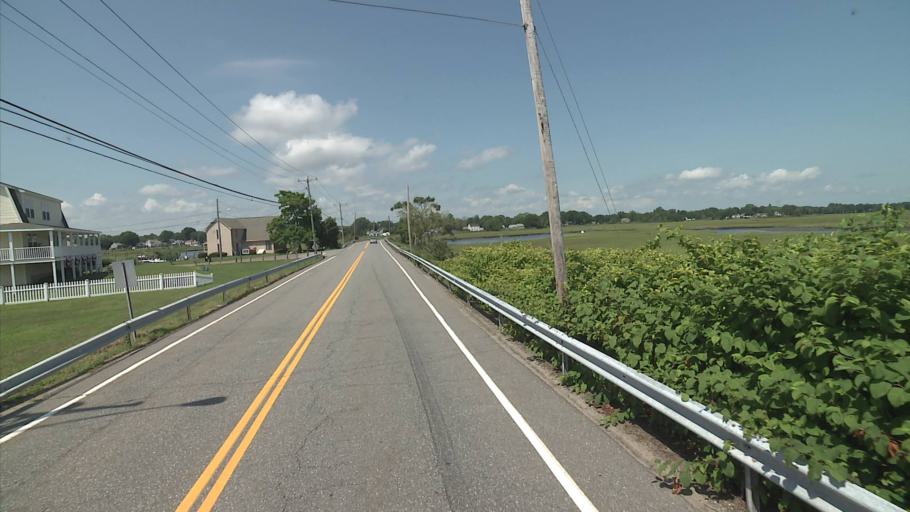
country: US
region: Connecticut
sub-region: Middlesex County
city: Saybrook Manor
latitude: 41.2753
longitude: -72.3934
